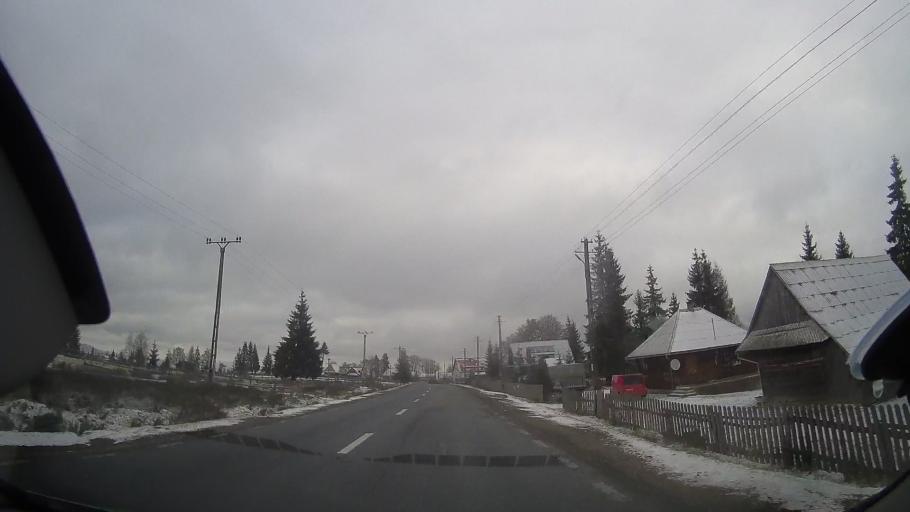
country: RO
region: Cluj
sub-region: Comuna Belis
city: Belis
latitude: 46.7049
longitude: 23.0378
